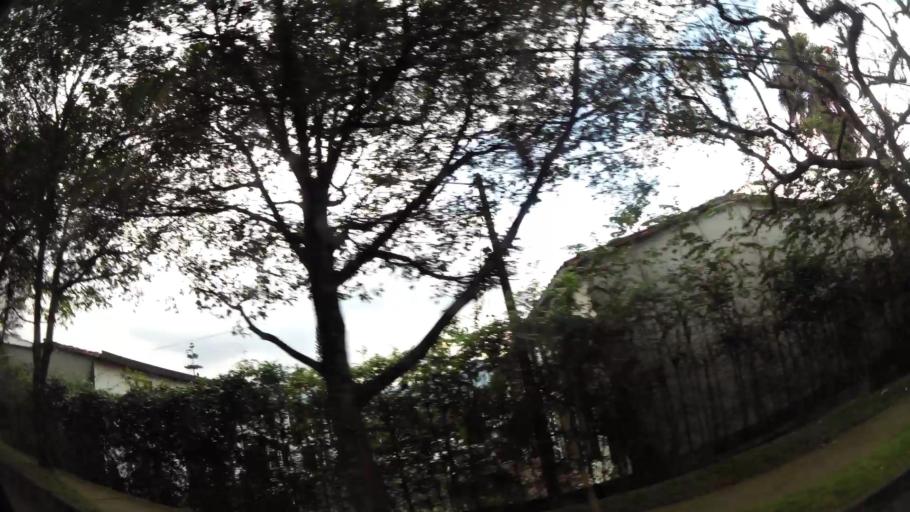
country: CO
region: Antioquia
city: Envigado
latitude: 6.1631
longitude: -75.5886
